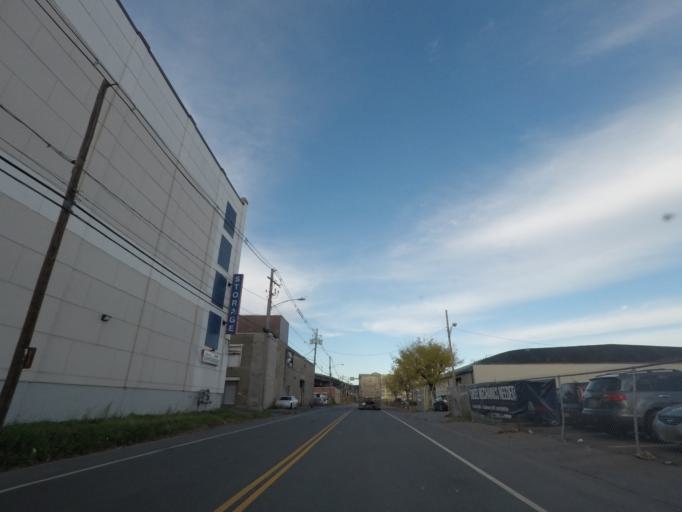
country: US
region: New York
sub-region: Rensselaer County
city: Rensselaer
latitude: 42.6380
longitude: -73.7533
